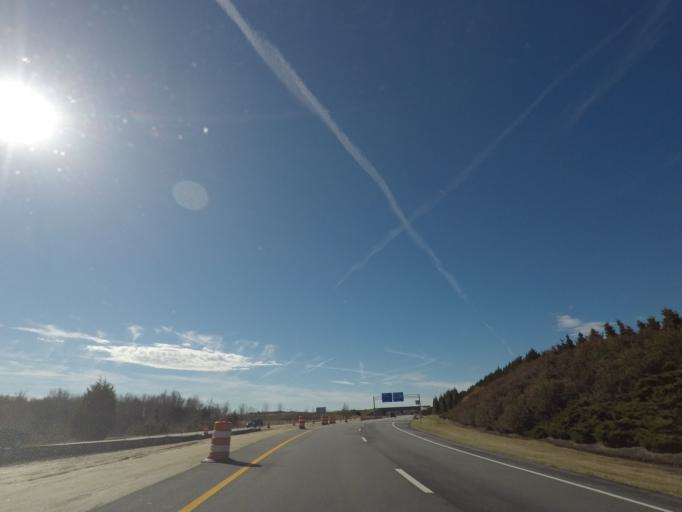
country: US
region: North Carolina
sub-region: Guilford County
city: Oak Ridge
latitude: 36.1176
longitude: -79.9336
